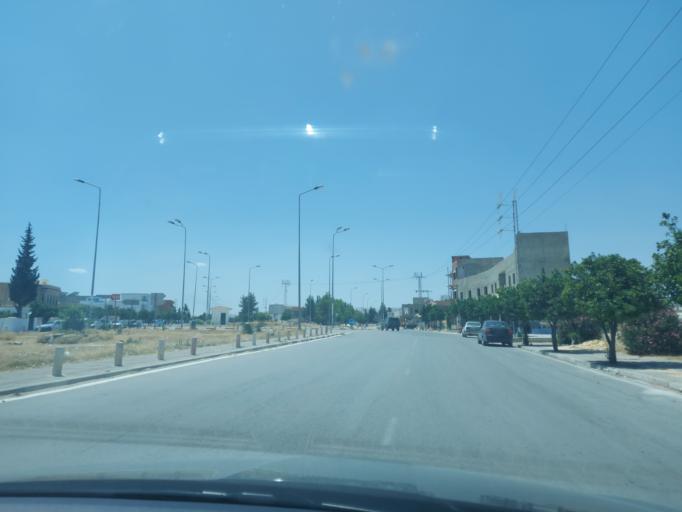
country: TN
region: Silyanah
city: Siliana
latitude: 36.0853
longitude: 9.3563
